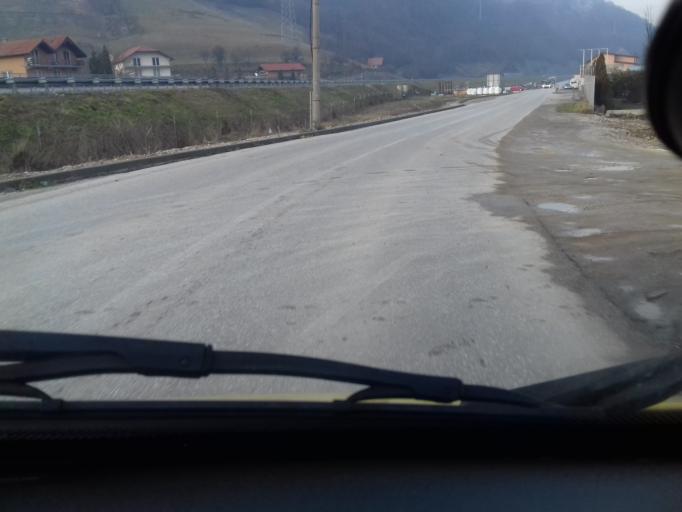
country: BA
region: Federation of Bosnia and Herzegovina
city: Dobrinje
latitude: 44.0552
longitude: 18.1042
